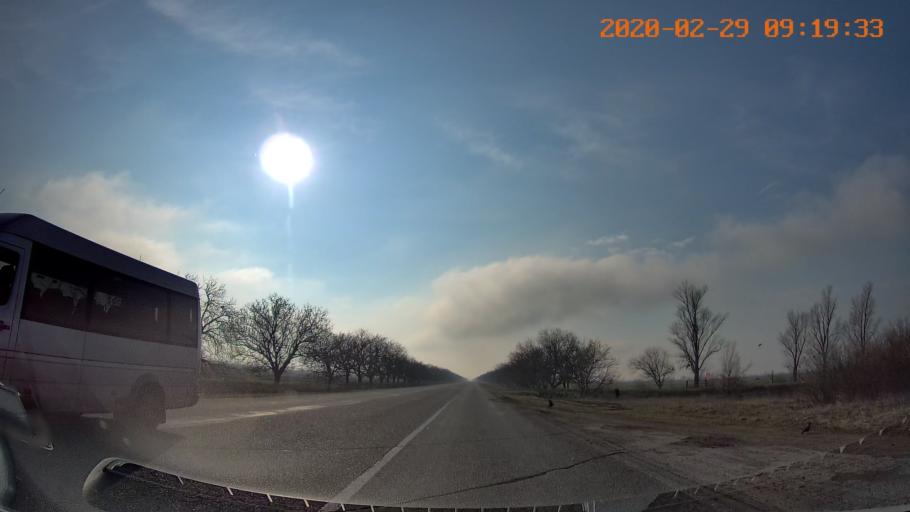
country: MD
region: Telenesti
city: Pervomaisc
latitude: 46.7613
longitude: 29.9405
